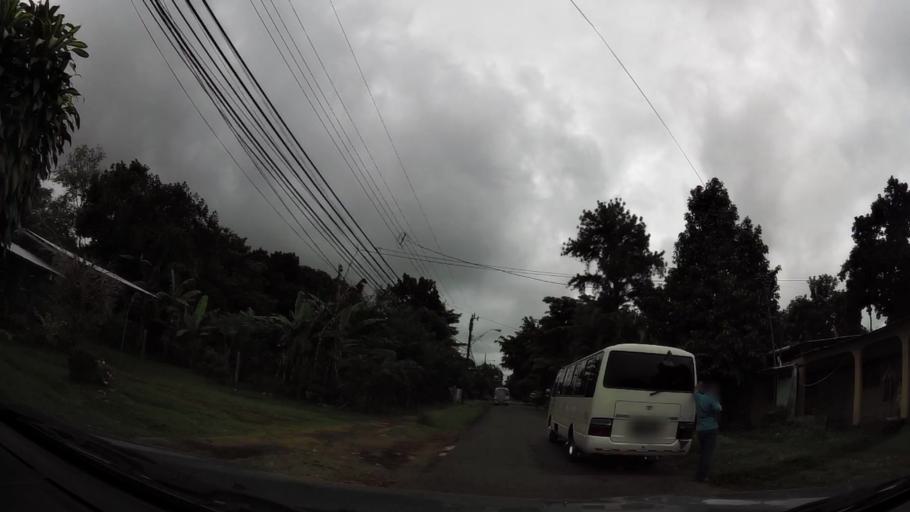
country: PA
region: Chiriqui
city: Dolega District
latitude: 8.5657
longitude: -82.4131
